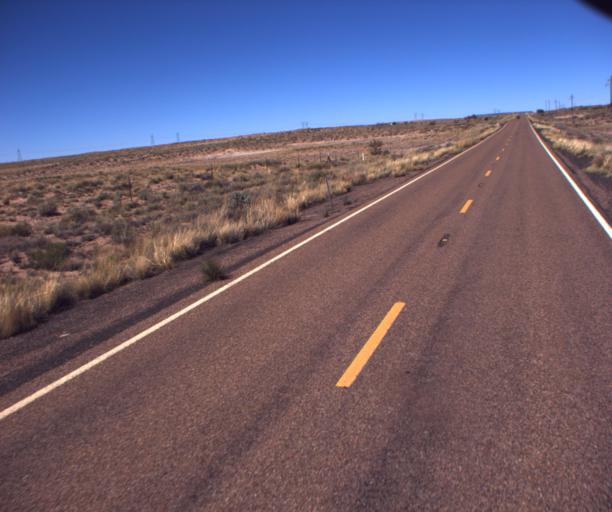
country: US
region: Arizona
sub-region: Navajo County
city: Holbrook
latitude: 35.1335
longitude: -110.0908
